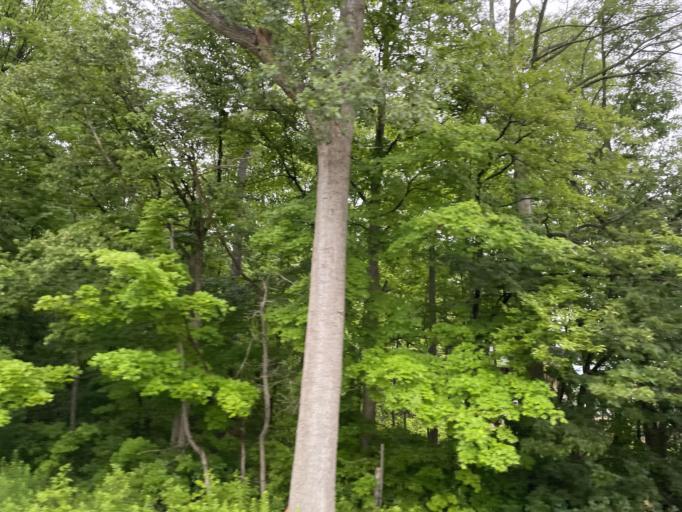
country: CA
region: Ontario
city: Cambridge
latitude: 43.4423
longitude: -80.2653
